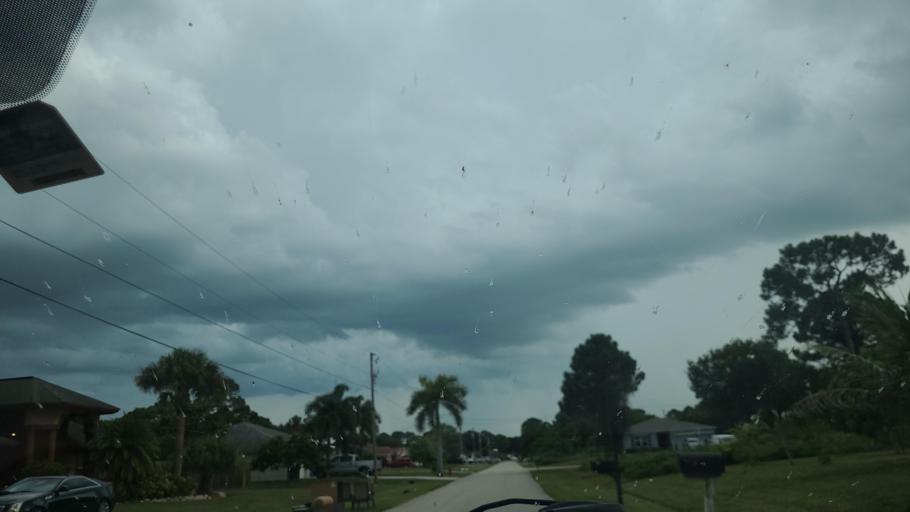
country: US
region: Florida
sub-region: Saint Lucie County
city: Port Saint Lucie
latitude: 27.2521
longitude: -80.4024
